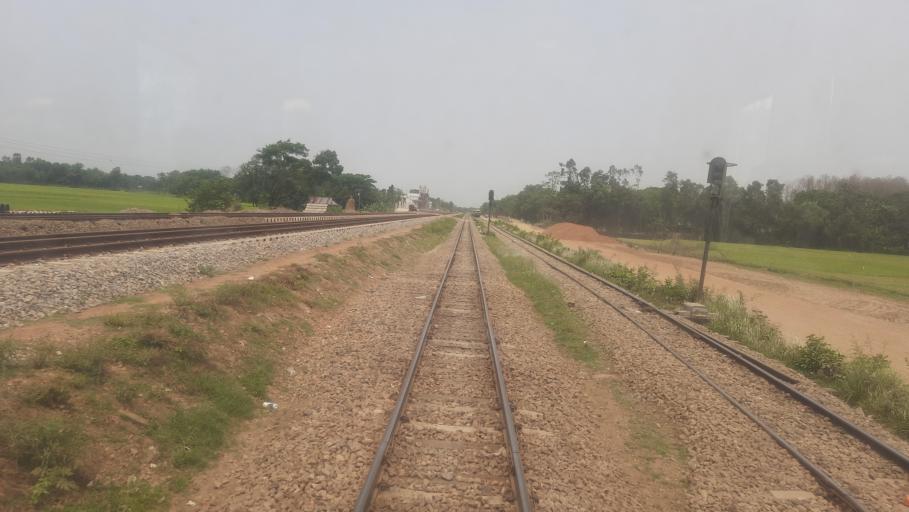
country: IN
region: Tripura
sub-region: West Tripura
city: Agartala
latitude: 23.6856
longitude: 91.1543
